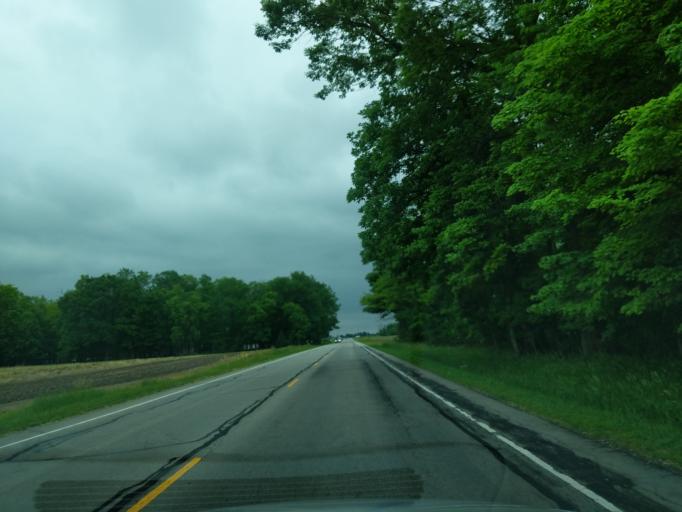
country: US
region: Indiana
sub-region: Madison County
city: Alexandria
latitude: 40.2772
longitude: -85.6033
